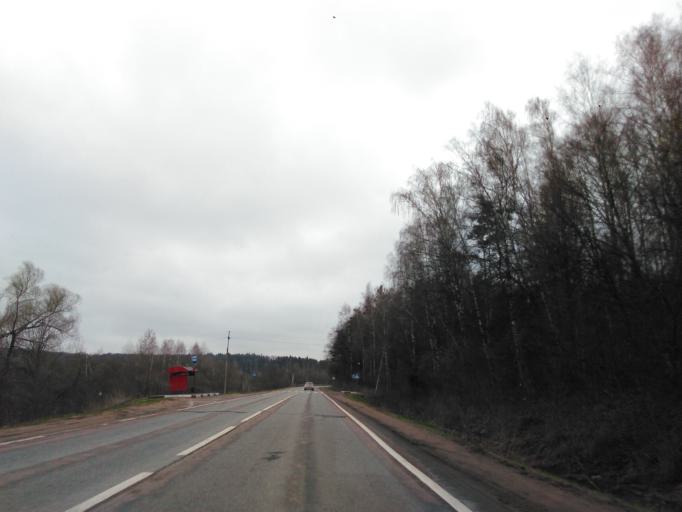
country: RU
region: Moskovskaya
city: Snegiri
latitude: 55.8484
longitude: 36.9547
